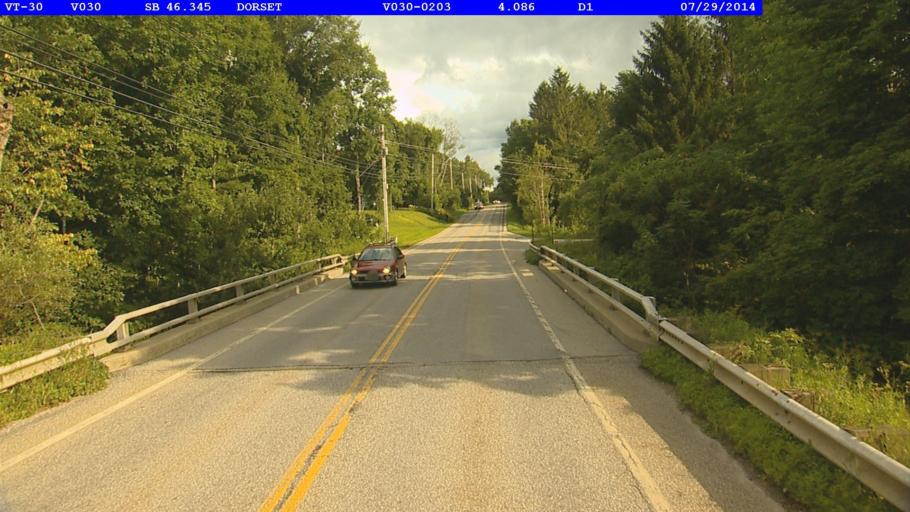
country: US
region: Vermont
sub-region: Bennington County
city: Manchester Center
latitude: 43.2638
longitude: -73.1054
